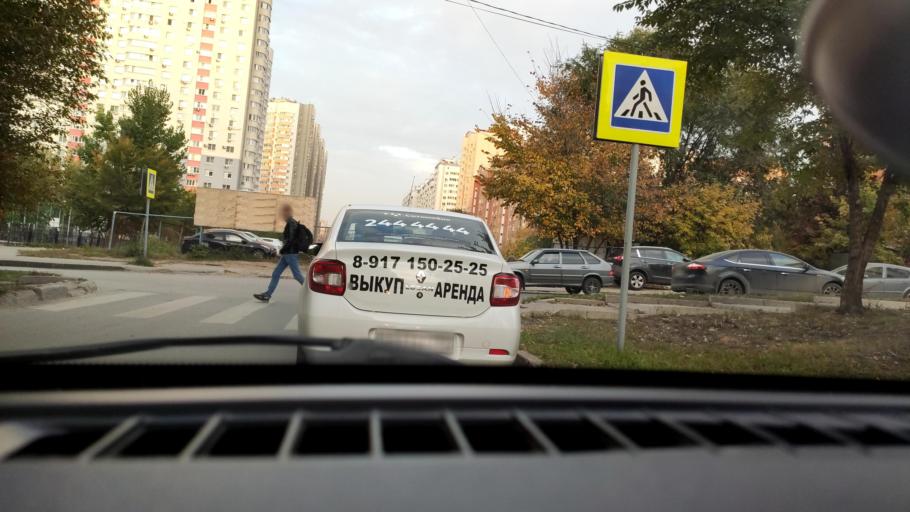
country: RU
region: Samara
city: Samara
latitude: 53.2153
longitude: 50.1652
